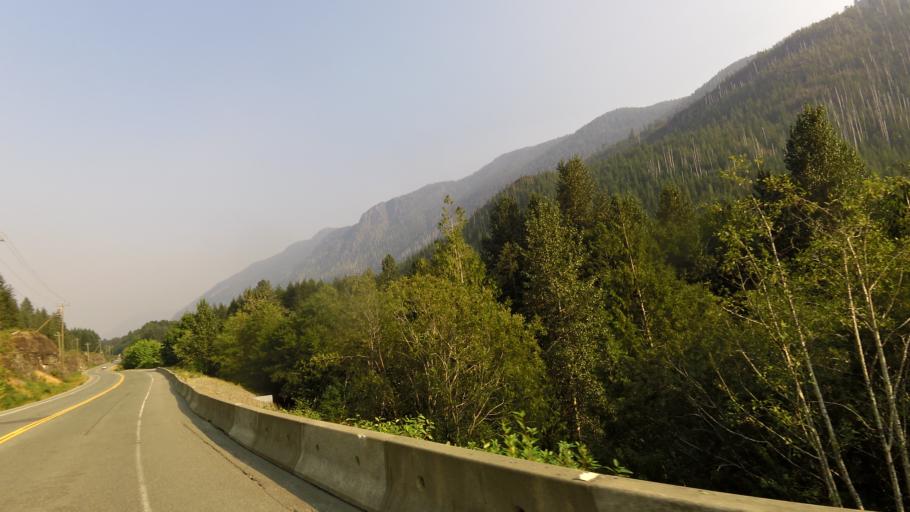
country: CA
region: British Columbia
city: Cumberland
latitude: 49.2971
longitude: -125.2823
